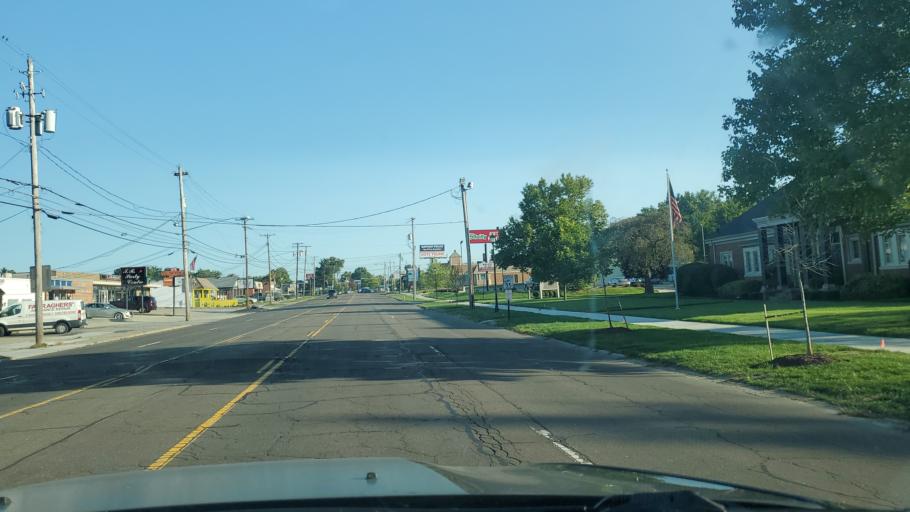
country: US
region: Ohio
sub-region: Mahoning County
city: Boardman
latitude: 41.0560
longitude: -80.6628
